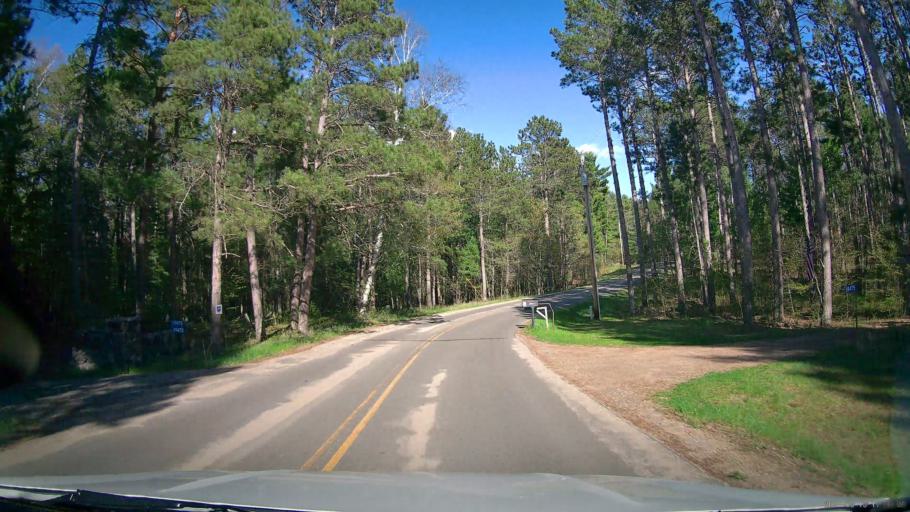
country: US
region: Minnesota
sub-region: Hubbard County
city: Park Rapids
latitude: 46.9926
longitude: -94.9579
